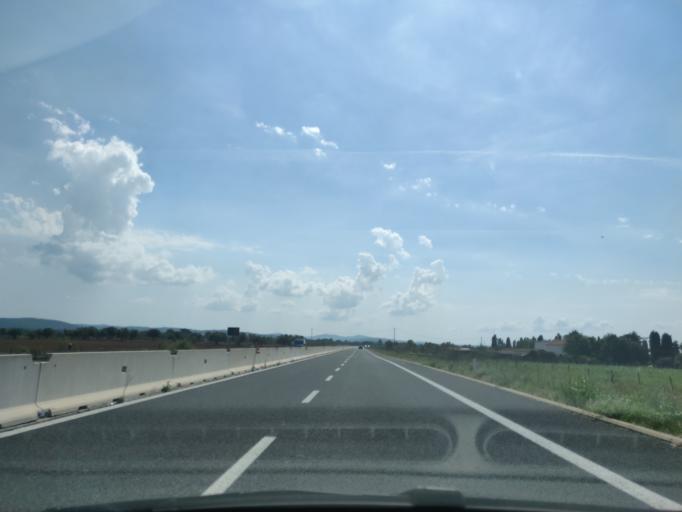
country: IT
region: Latium
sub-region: Provincia di Viterbo
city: Blera
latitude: 42.3271
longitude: 11.9869
